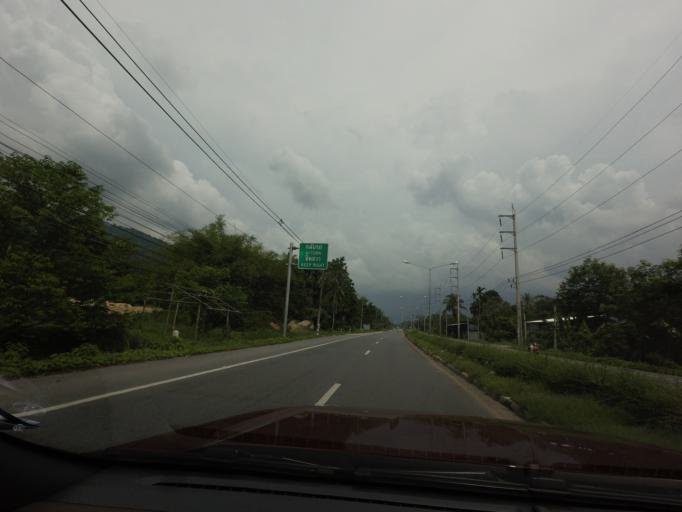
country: TH
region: Yala
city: Yala
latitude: 6.4886
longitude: 101.2653
